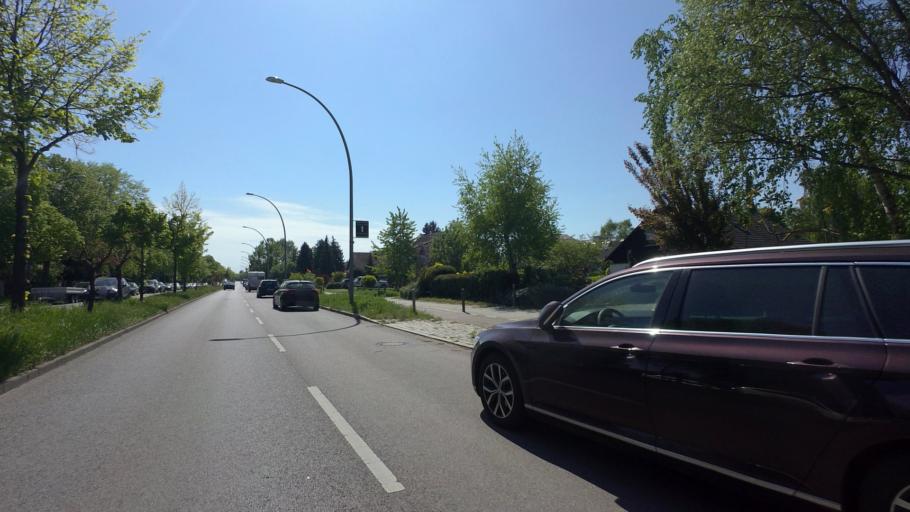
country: DE
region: Berlin
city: Rudow
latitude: 52.4089
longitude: 13.5062
